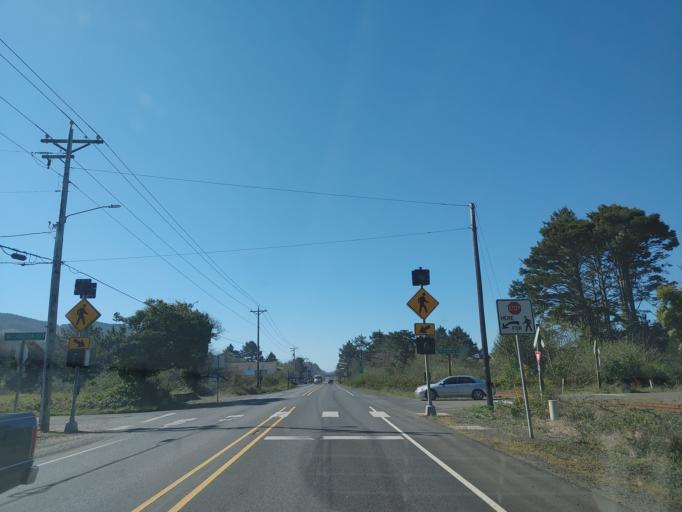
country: US
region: Oregon
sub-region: Tillamook County
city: Rockaway Beach
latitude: 45.6004
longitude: -123.9461
